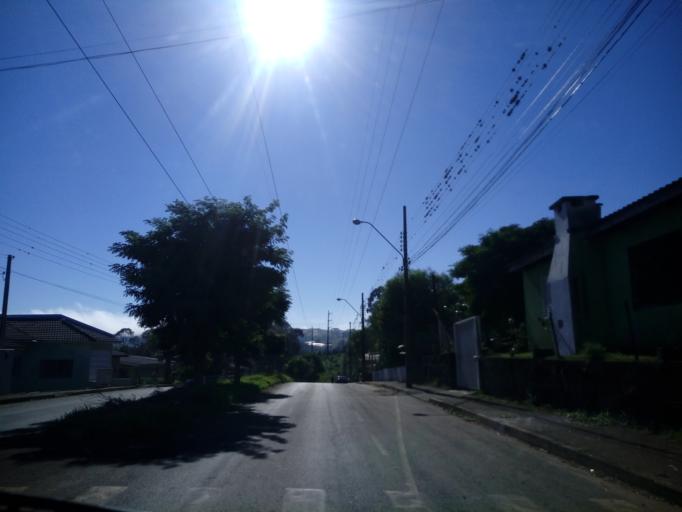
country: BR
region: Santa Catarina
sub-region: Chapeco
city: Chapeco
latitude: -27.0656
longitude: -52.6038
